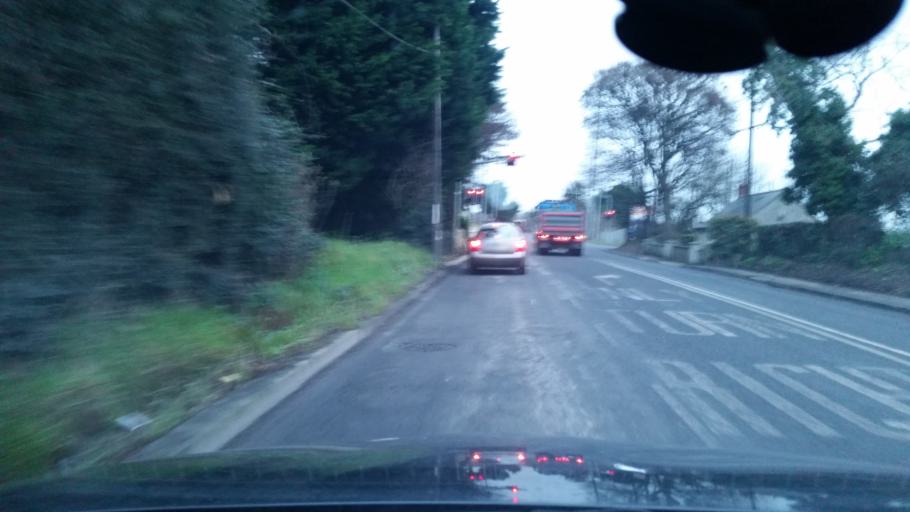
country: IE
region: Leinster
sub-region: Dublin City
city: Finglas
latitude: 53.4226
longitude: -6.3258
